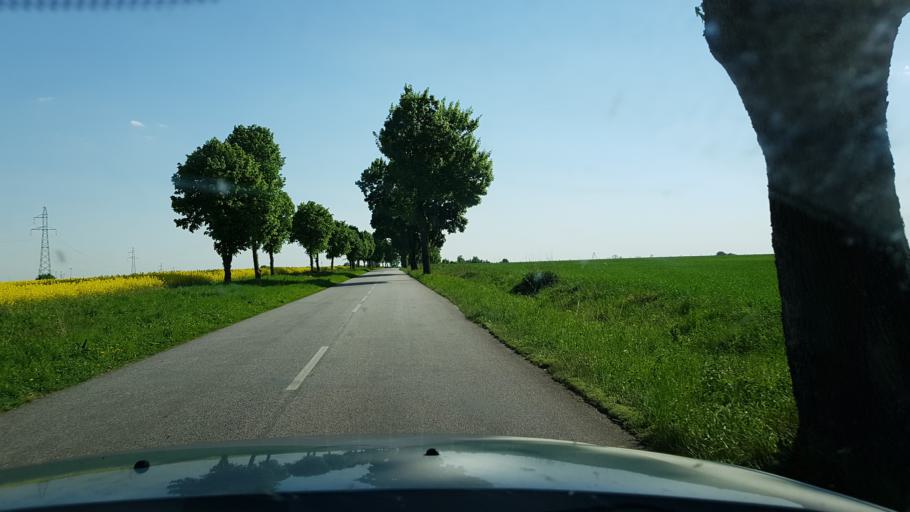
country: PL
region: West Pomeranian Voivodeship
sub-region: Powiat lobeski
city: Resko
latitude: 53.7960
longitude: 15.4142
